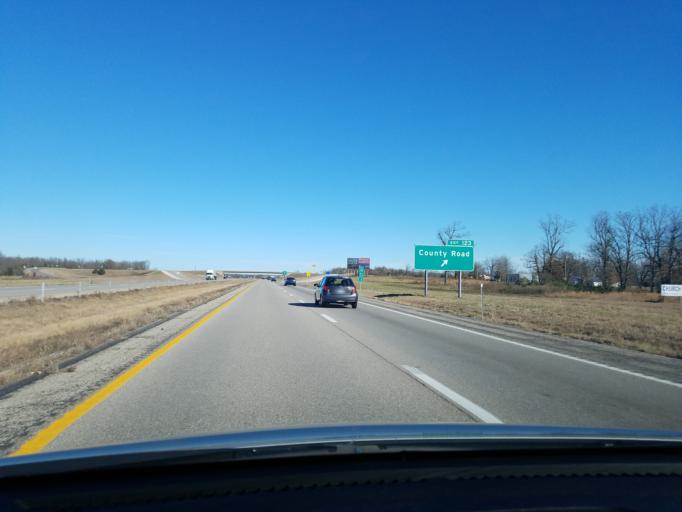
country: US
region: Missouri
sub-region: Laclede County
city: Lebanon
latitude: 37.5970
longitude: -92.7201
